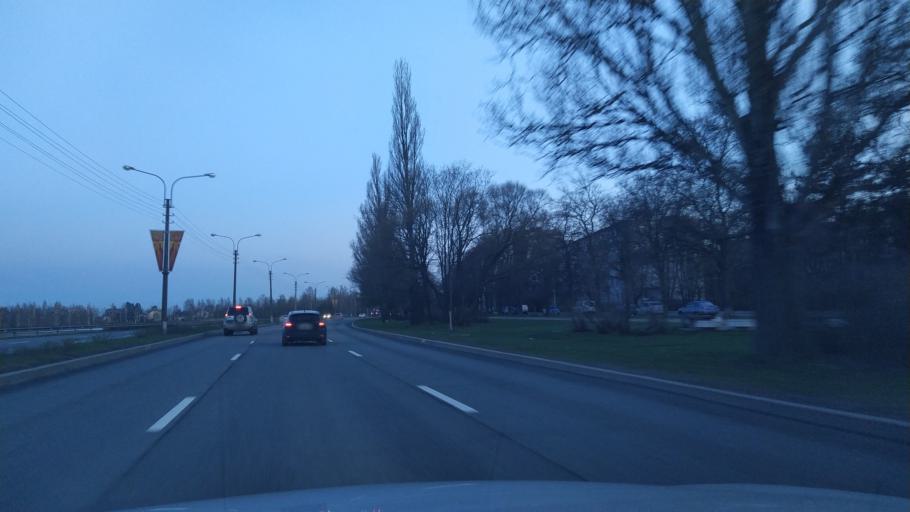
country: RU
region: St.-Petersburg
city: Sestroretsk
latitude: 60.0985
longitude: 29.9803
